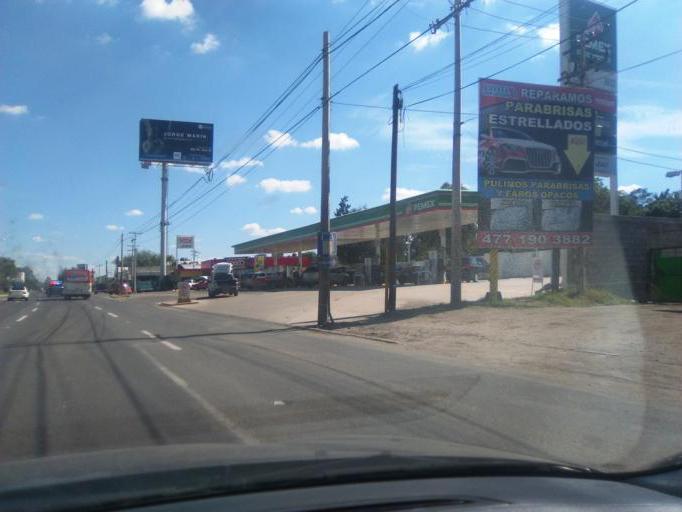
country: MX
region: Guanajuato
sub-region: Leon
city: Fraccionamiento Paraiso Real
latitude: 21.0810
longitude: -101.6093
